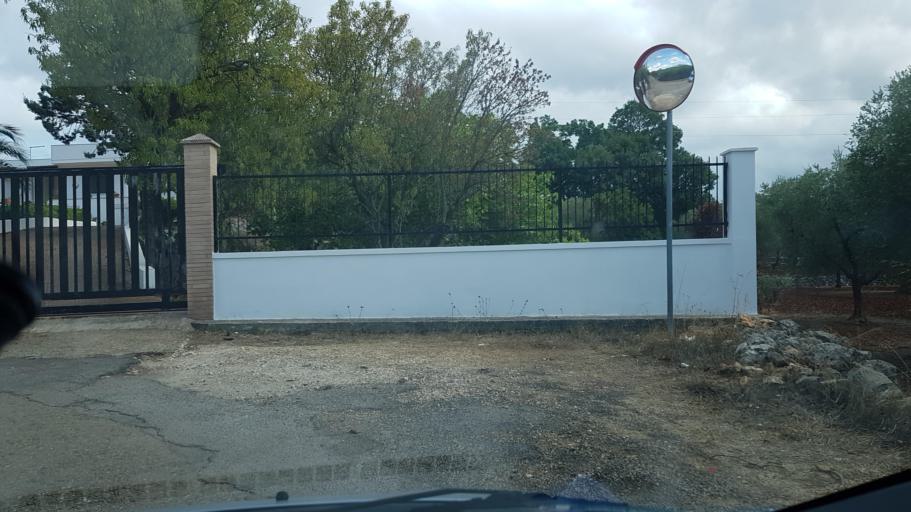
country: IT
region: Apulia
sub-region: Provincia di Brindisi
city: San Vito dei Normanni
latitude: 40.6673
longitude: 17.7196
